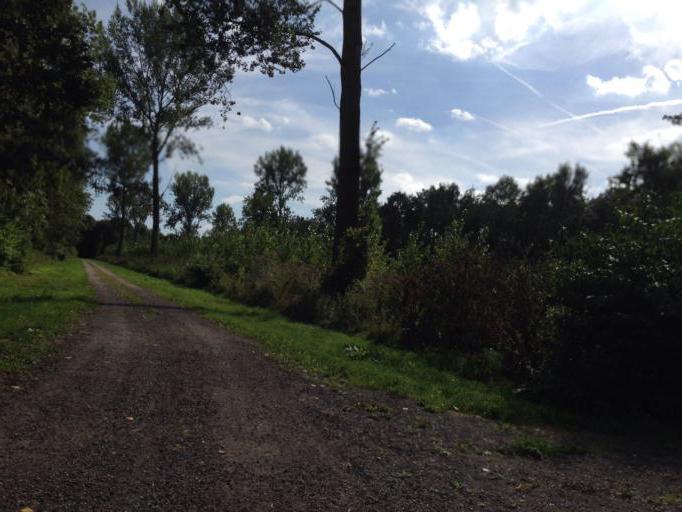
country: NL
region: North Holland
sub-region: Gemeente Huizen
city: Huizen
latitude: 52.3470
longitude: 5.2667
